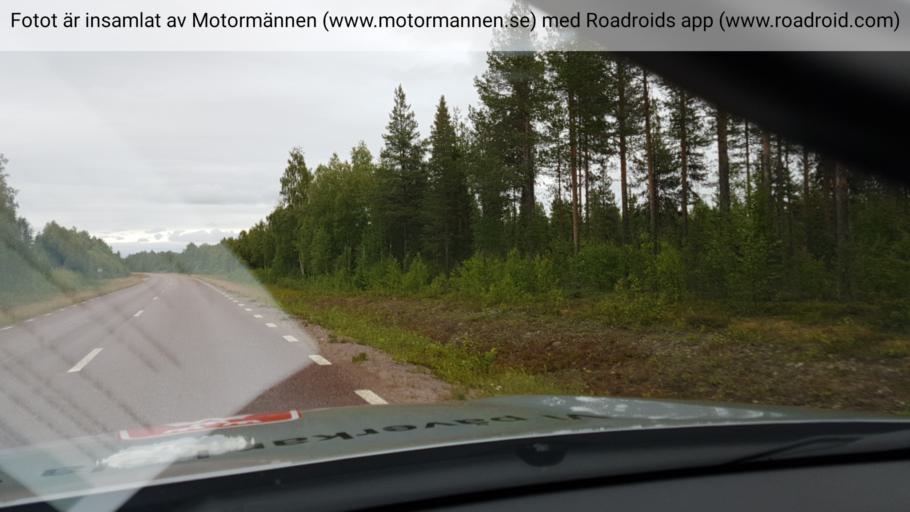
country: SE
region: Norrbotten
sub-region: Pajala Kommun
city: Pajala
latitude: 67.1472
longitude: 22.6237
